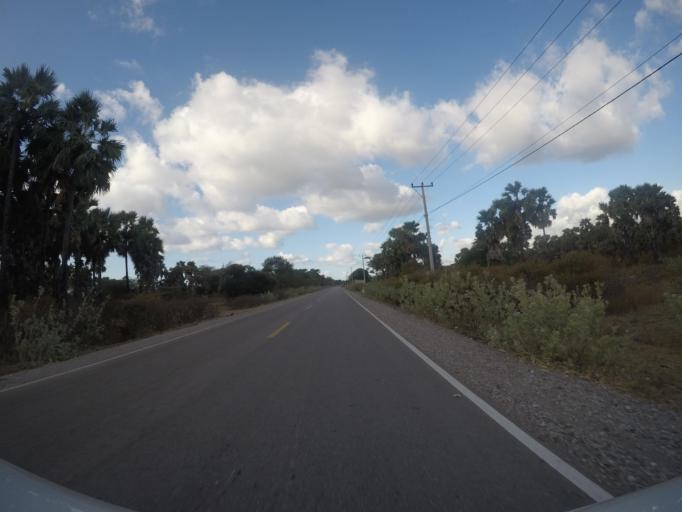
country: TL
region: Lautem
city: Lospalos
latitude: -8.3833
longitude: 126.8594
